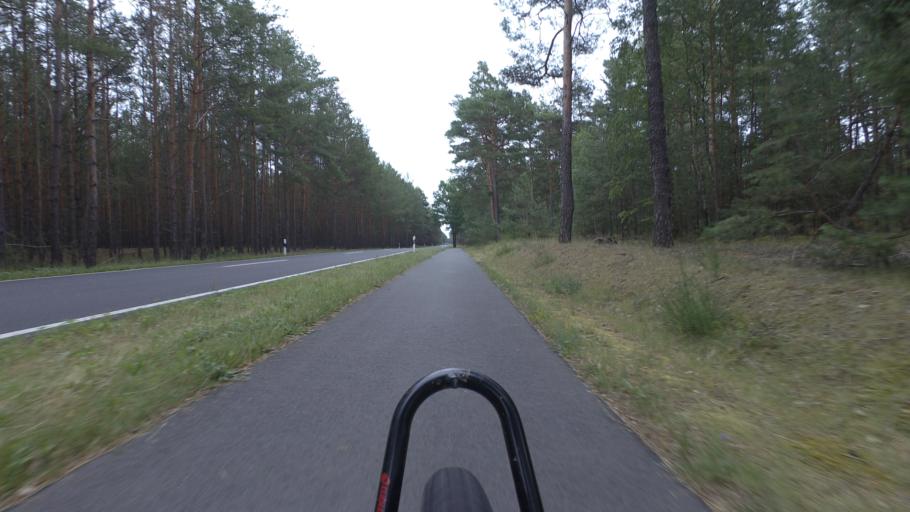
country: DE
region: Brandenburg
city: Sperenberg
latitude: 52.0873
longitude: 13.2802
